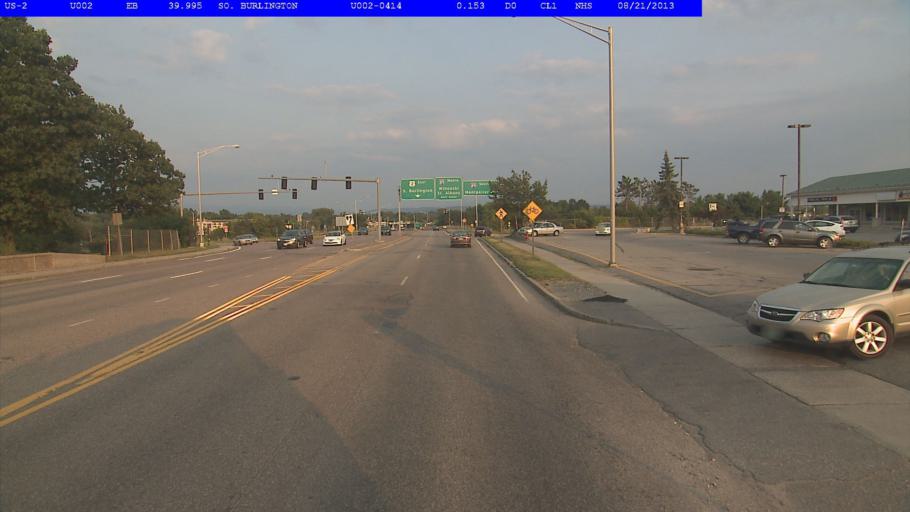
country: US
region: Vermont
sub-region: Chittenden County
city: South Burlington
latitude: 44.4712
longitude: -73.1876
